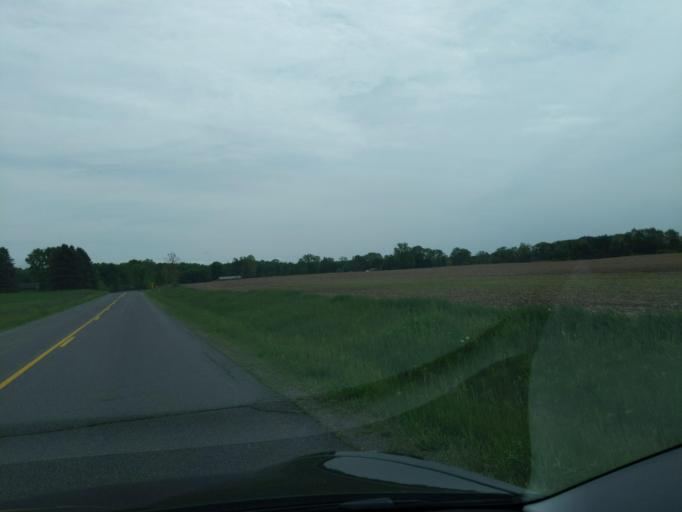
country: US
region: Michigan
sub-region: Ingham County
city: Stockbridge
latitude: 42.4304
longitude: -84.2241
